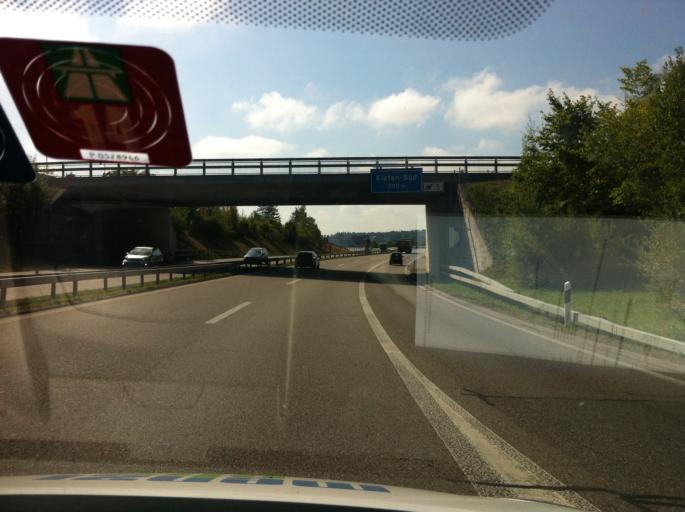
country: CH
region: Zurich
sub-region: Bezirk Buelach
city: Kloten / Freienberg (Chanzler-Chlini Chaseren)
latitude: 47.4620
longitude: 8.5749
